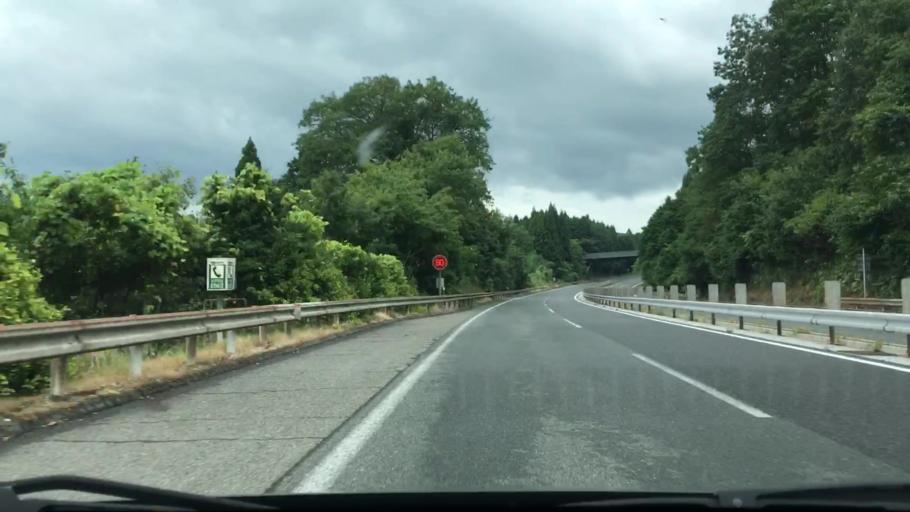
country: JP
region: Okayama
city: Niimi
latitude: 34.9329
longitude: 133.3279
